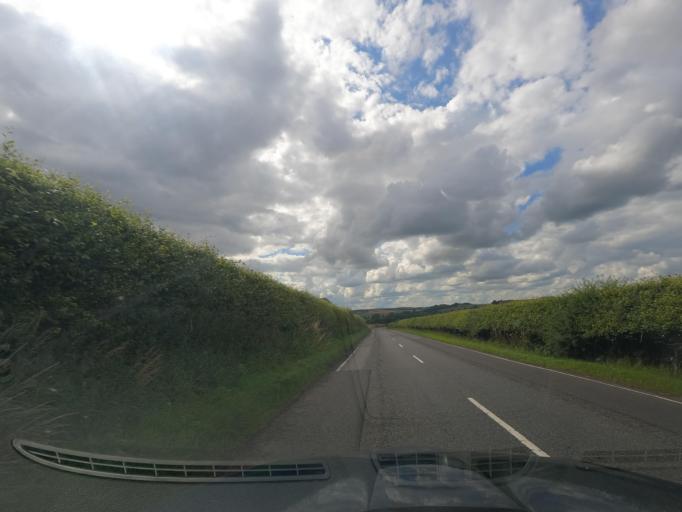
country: GB
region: Scotland
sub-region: The Scottish Borders
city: Kelso
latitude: 55.7043
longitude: -2.4459
